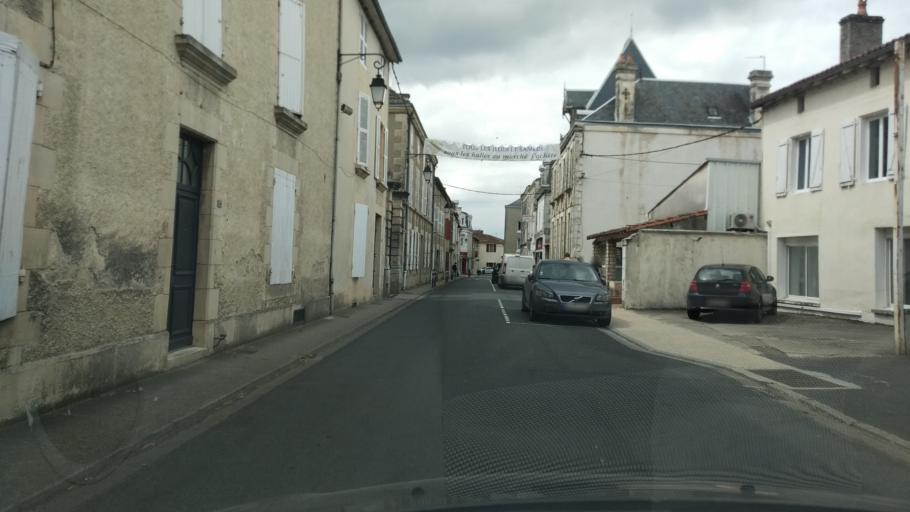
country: FR
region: Poitou-Charentes
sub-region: Departement de la Vienne
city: Saint-Maurice-la-Clouere
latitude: 46.3724
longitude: 0.4054
